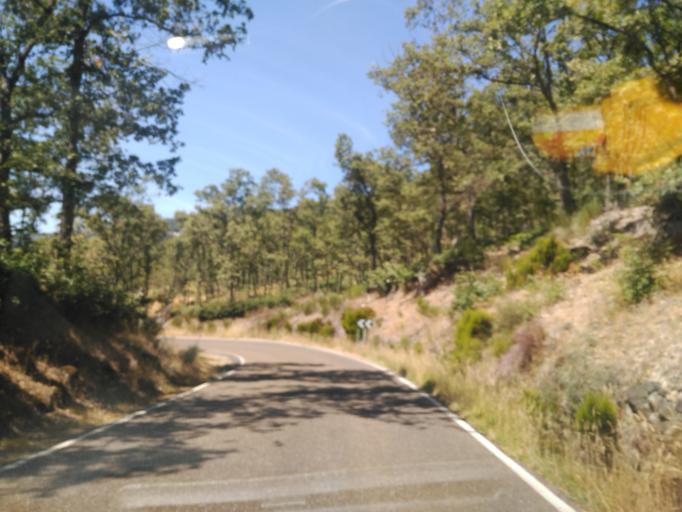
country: ES
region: Castille and Leon
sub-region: Provincia de Zamora
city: Galende
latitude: 42.1320
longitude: -6.6981
